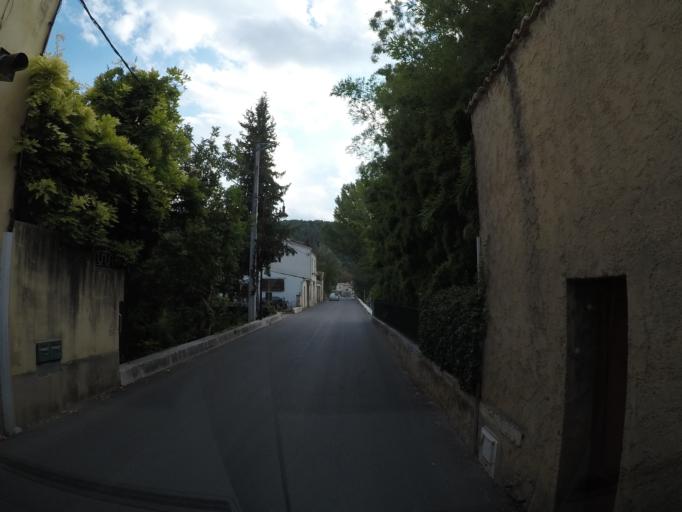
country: FR
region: Provence-Alpes-Cote d'Azur
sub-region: Departement des Alpes-de-Haute-Provence
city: Riez
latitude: 43.8178
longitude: 6.0904
